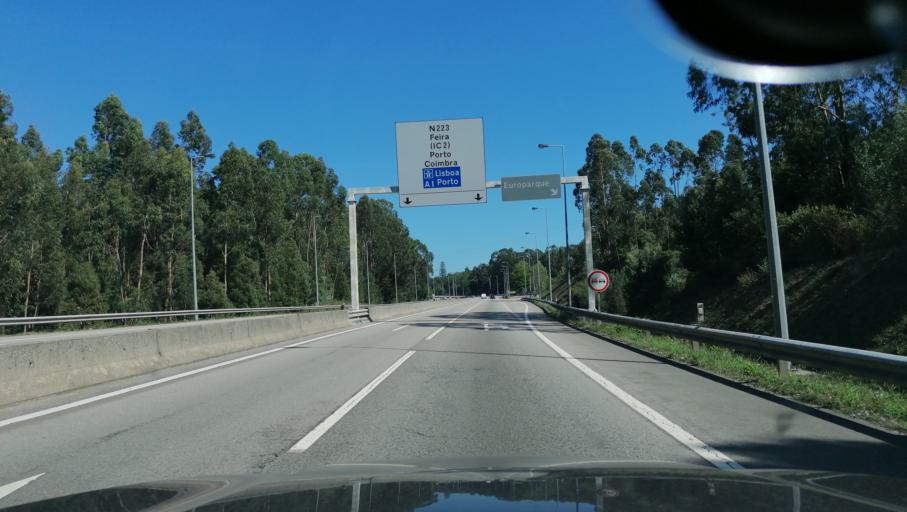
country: PT
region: Aveiro
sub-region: Santa Maria da Feira
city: Rio Meao
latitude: 40.9260
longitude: -8.5835
